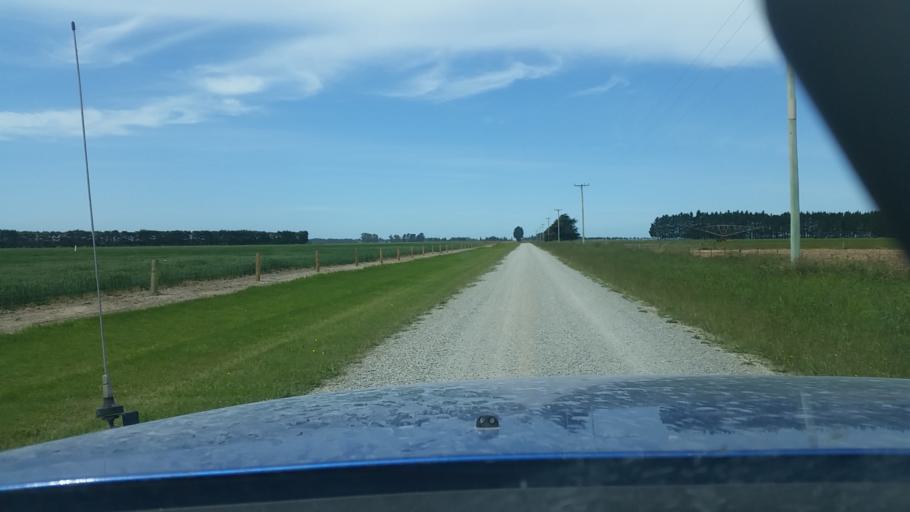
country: NZ
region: Canterbury
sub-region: Ashburton District
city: Tinwald
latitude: -44.0561
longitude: 171.7716
